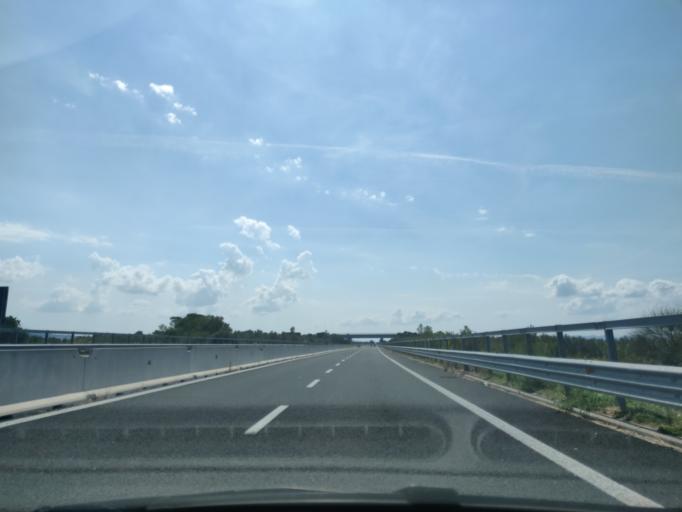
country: IT
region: Latium
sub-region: Provincia di Viterbo
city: Blera
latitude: 42.3195
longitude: 11.9906
